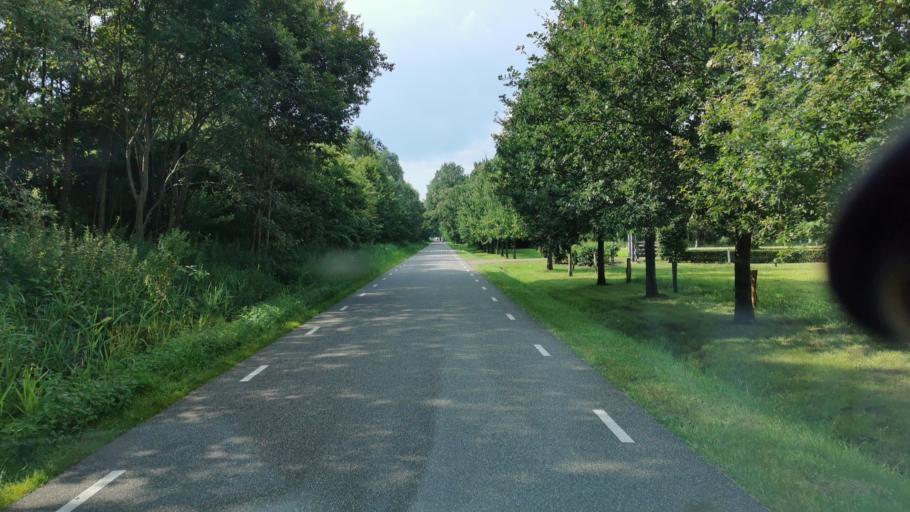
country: NL
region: Overijssel
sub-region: Gemeente Enschede
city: Enschede
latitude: 52.2403
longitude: 6.9485
